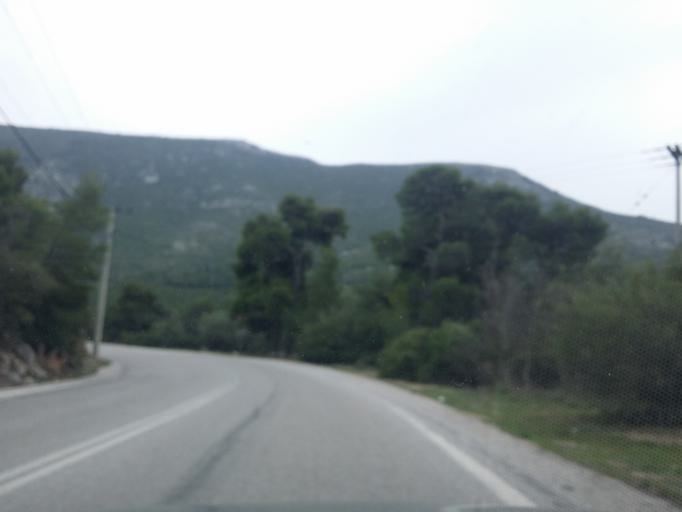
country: GR
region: Attica
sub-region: Nomarchia Dytikis Attikis
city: Vilia
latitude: 38.1470
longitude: 23.2472
